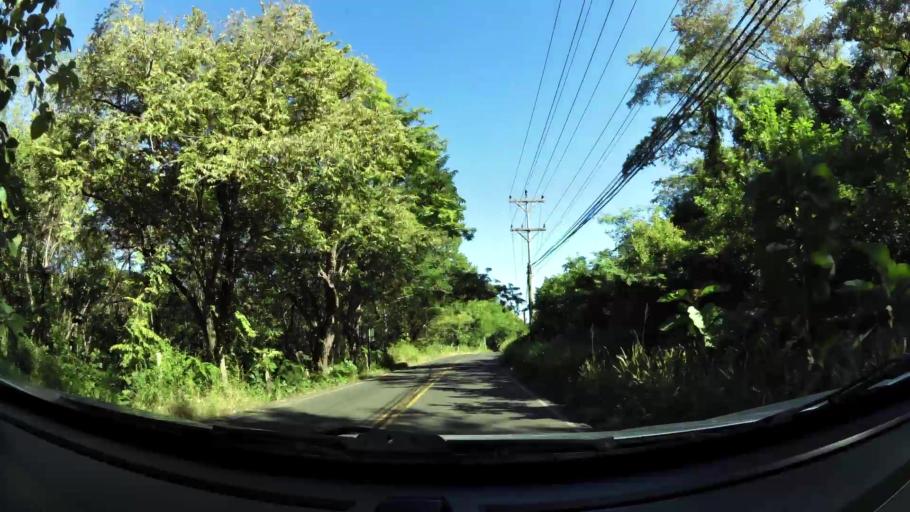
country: CR
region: Guanacaste
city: Sardinal
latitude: 10.4300
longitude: -85.7833
